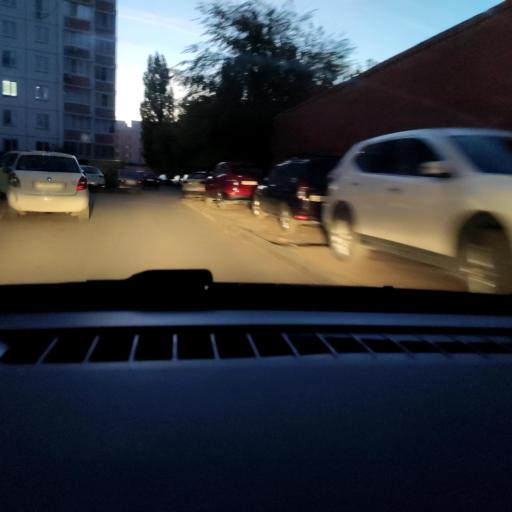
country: RU
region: Voronezj
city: Voronezh
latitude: 51.6452
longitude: 39.1253
